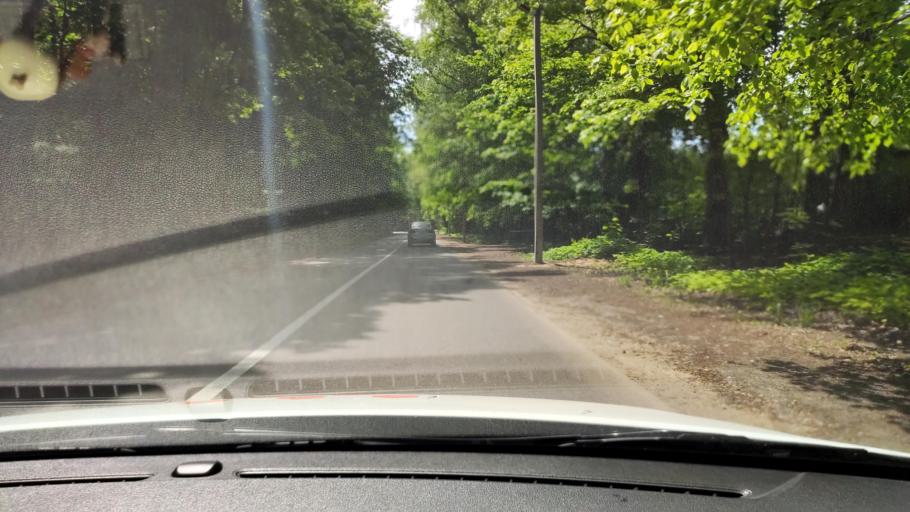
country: RU
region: Tatarstan
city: Osinovo
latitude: 55.8411
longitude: 48.8171
